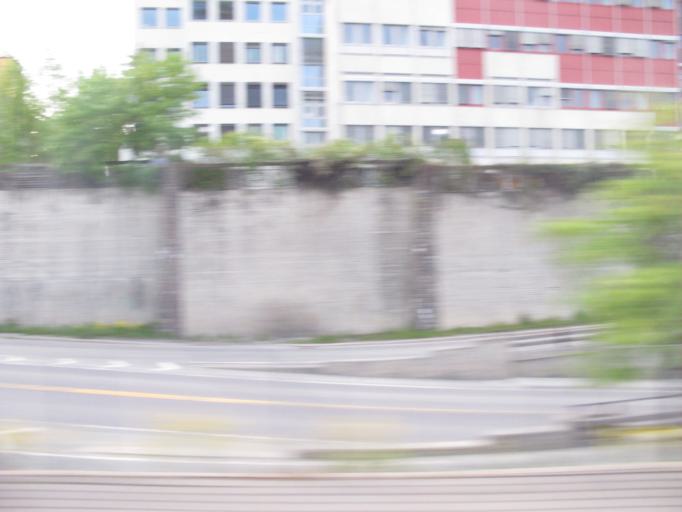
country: NO
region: Oppland
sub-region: Lillehammer
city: Lillehammer
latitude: 61.1163
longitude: 10.4609
